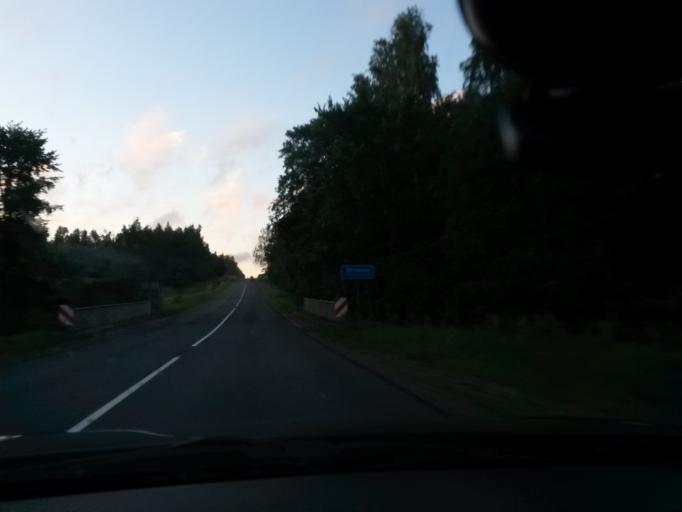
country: LV
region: Madonas Rajons
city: Madona
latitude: 56.7757
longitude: 26.0307
